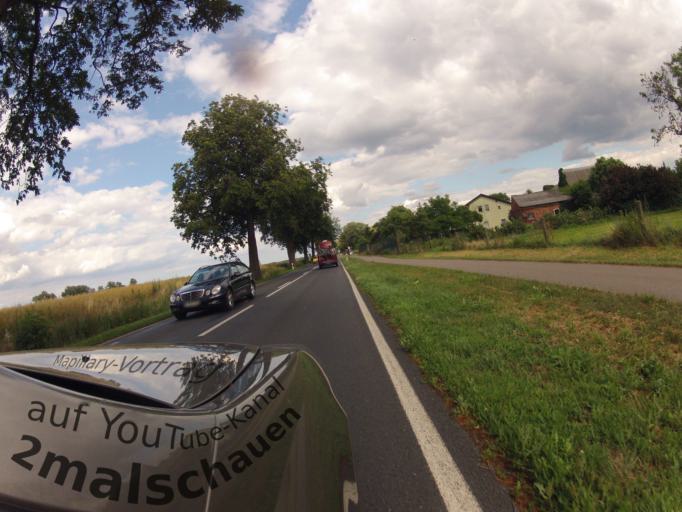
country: DE
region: Mecklenburg-Vorpommern
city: Usedom
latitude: 53.8732
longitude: 13.8772
